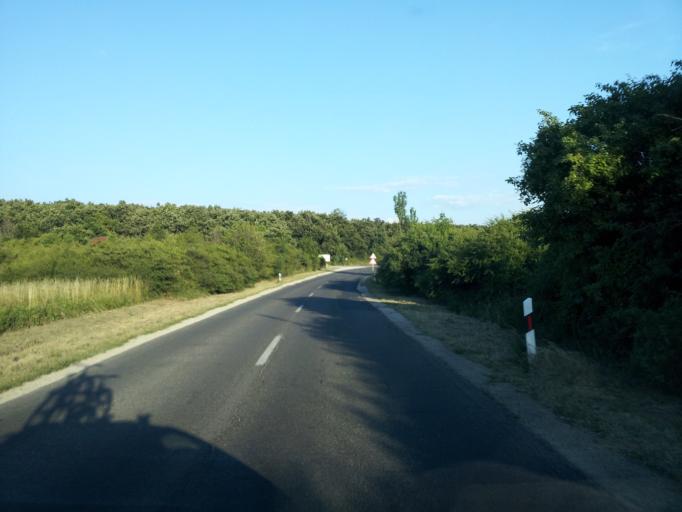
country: HU
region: Veszprem
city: Szentkiralyszabadja
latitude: 47.0627
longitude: 17.9891
